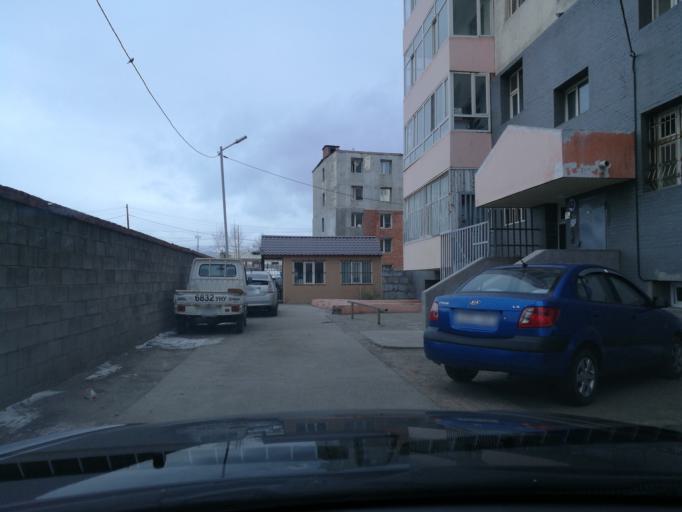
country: MN
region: Ulaanbaatar
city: Ulaanbaatar
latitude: 47.9293
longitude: 106.9124
